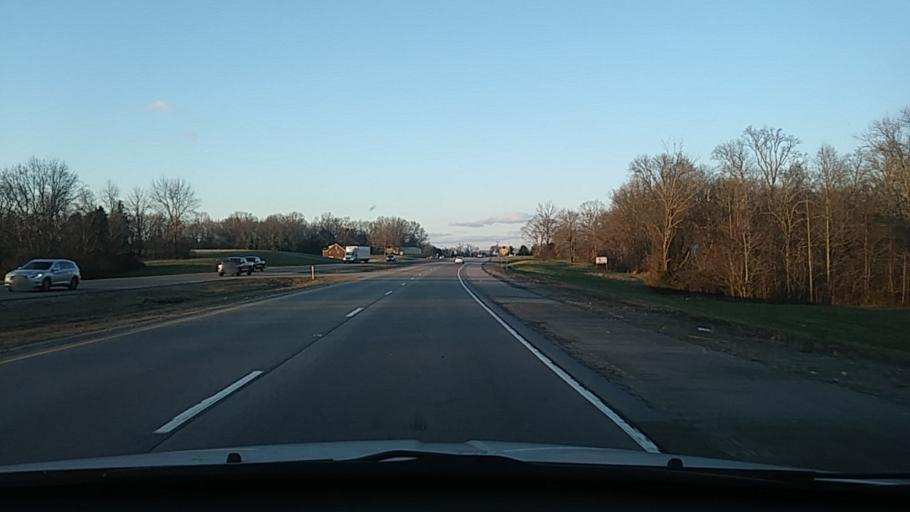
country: US
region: Tennessee
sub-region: Sumner County
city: Portland
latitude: 36.5383
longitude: -86.5078
